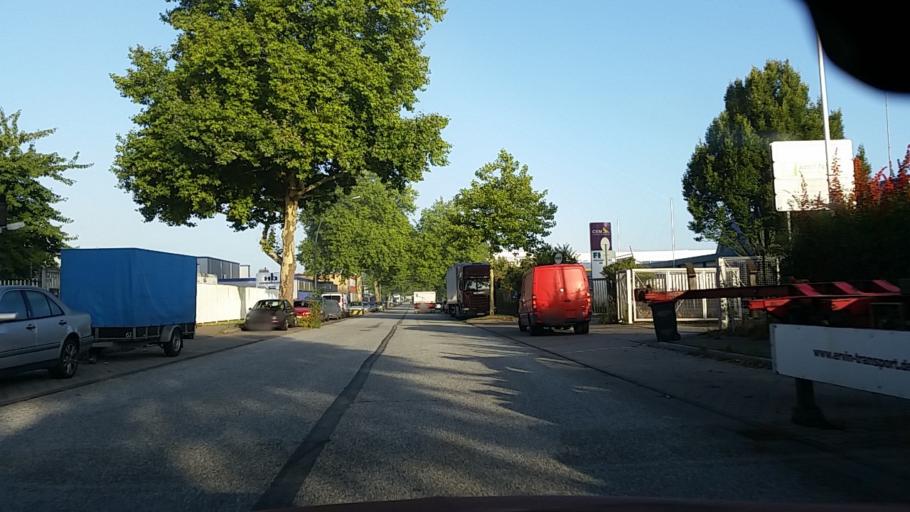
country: DE
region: Hamburg
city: Wandsbek
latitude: 53.5218
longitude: 10.0973
